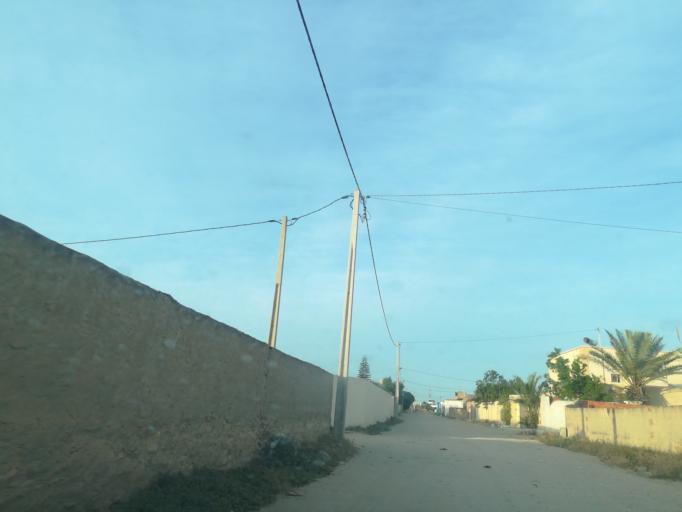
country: TN
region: Safaqis
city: Al Qarmadah
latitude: 34.8226
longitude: 10.7564
